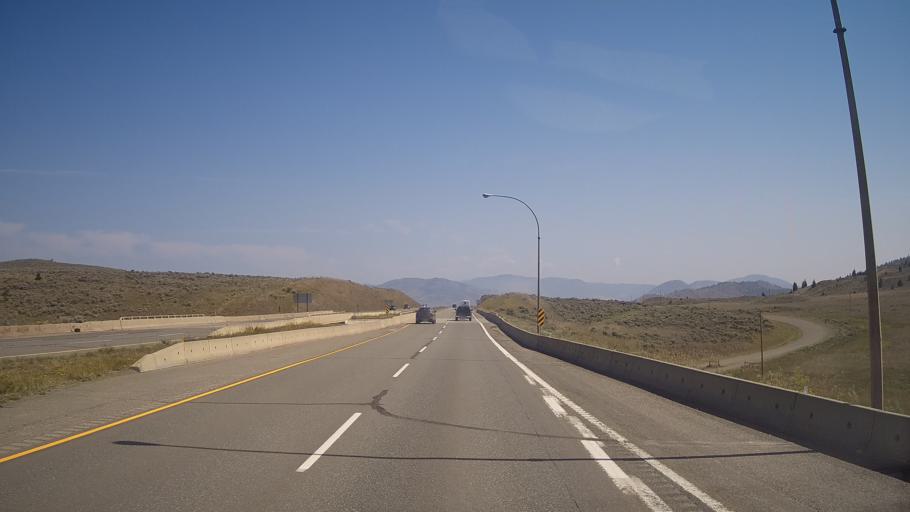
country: CA
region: British Columbia
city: Kamloops
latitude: 50.6555
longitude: -120.4774
